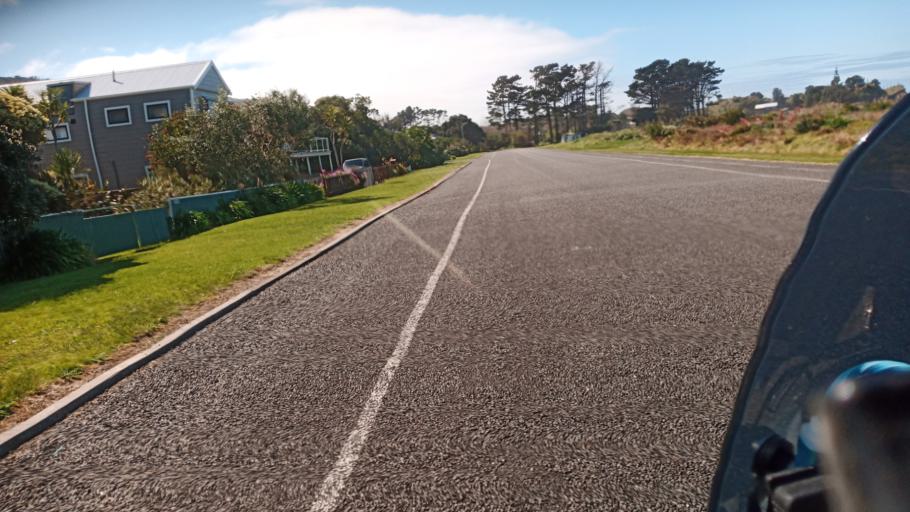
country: NZ
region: Gisborne
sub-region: Gisborne District
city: Gisborne
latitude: -39.0163
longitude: 177.8853
